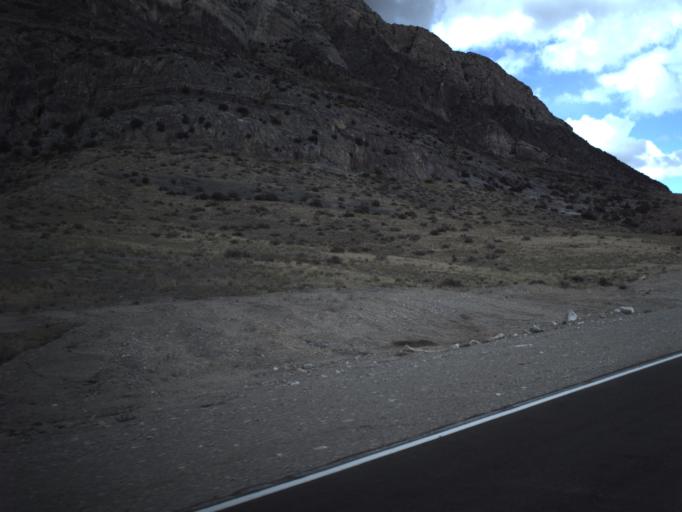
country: US
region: Utah
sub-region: Beaver County
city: Milford
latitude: 38.5059
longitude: -113.6022
